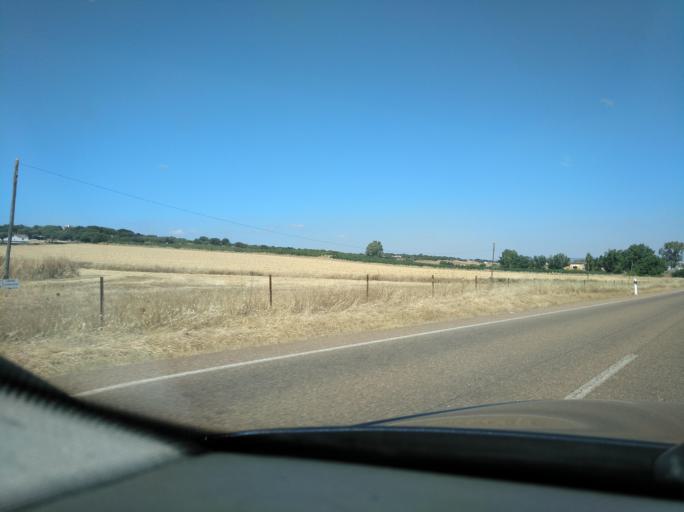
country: ES
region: Extremadura
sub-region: Provincia de Badajoz
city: Olivenza
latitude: 38.7001
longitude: -7.1065
